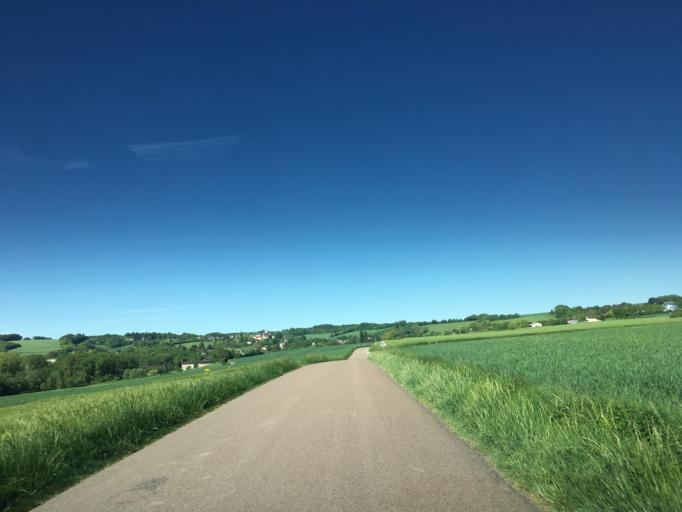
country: FR
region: Bourgogne
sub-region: Departement de l'Yonne
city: Aillant-sur-Tholon
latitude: 47.8258
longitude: 3.3283
